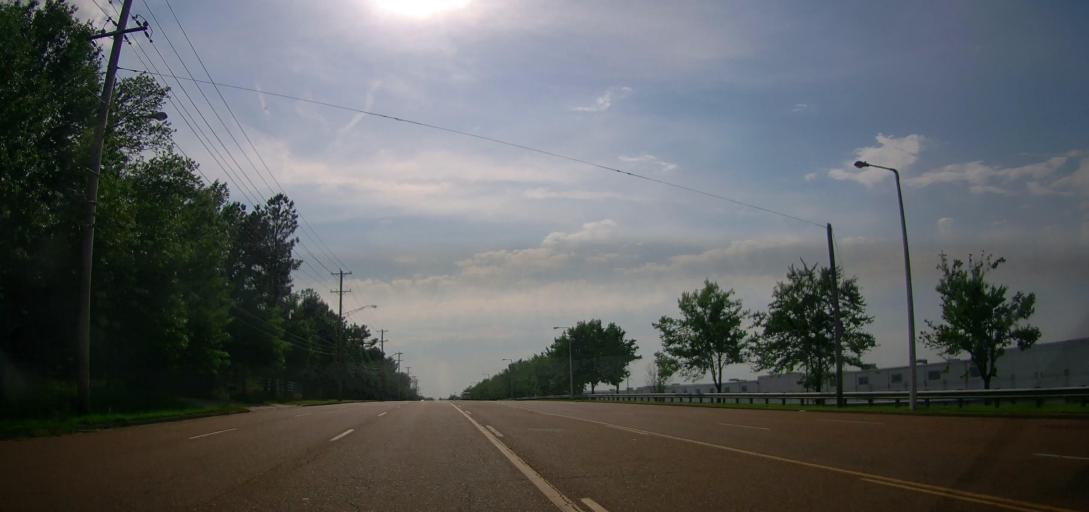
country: US
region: Mississippi
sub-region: De Soto County
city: Olive Branch
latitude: 35.0058
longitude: -89.8530
